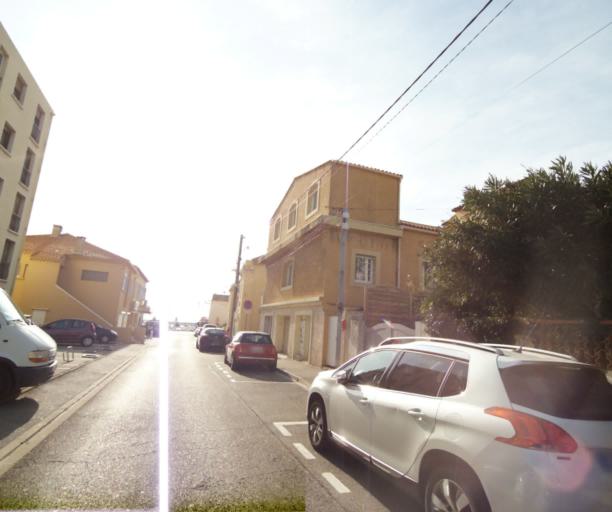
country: FR
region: Provence-Alpes-Cote d'Azur
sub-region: Departement des Bouches-du-Rhone
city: Carry-le-Rouet
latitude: 43.3313
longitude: 5.1513
